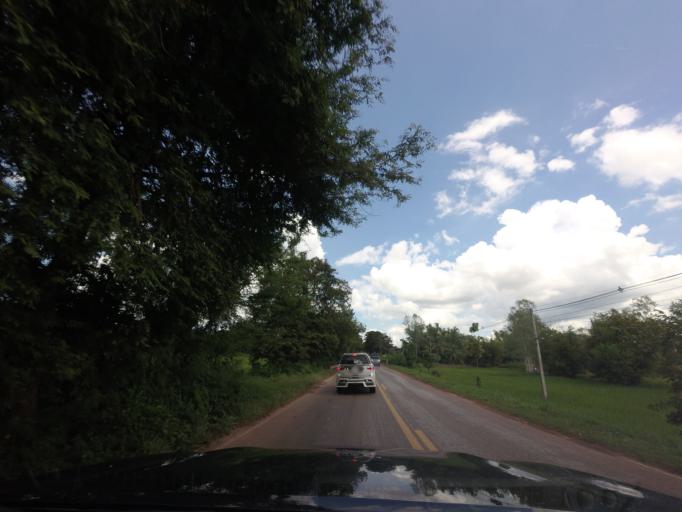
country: TH
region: Changwat Udon Thani
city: Ban Dung
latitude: 17.6556
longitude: 103.1425
